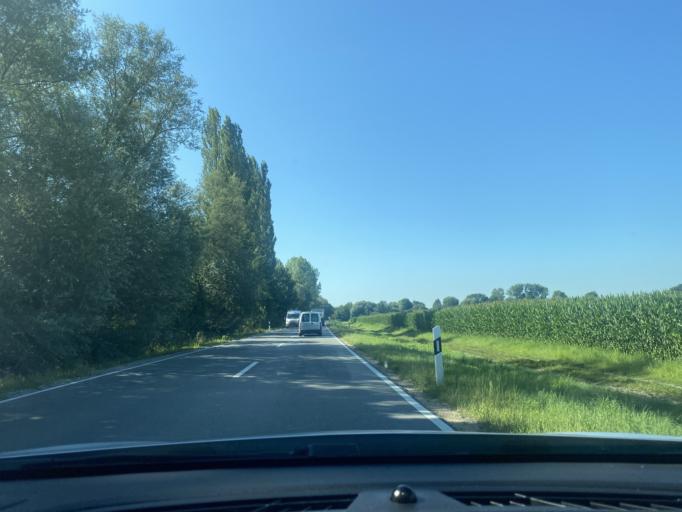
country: DE
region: Bavaria
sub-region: Upper Bavaria
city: Eitting
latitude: 48.3592
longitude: 11.8995
